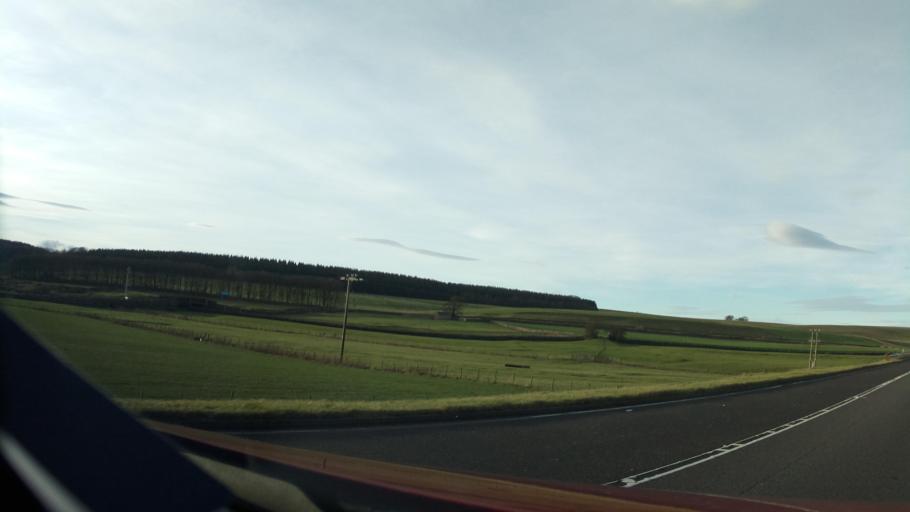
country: GB
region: England
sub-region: Cumbria
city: Penrith
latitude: 54.5616
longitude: -2.6800
